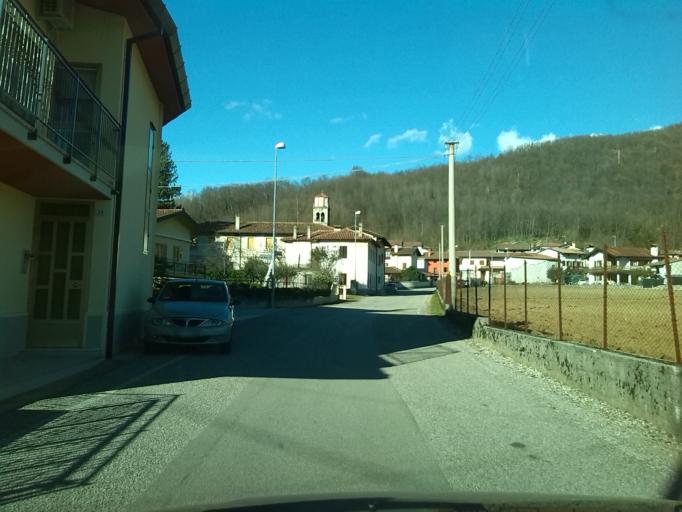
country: IT
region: Friuli Venezia Giulia
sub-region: Provincia di Udine
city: San Pietro al Natisone
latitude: 46.1005
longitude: 13.4742
